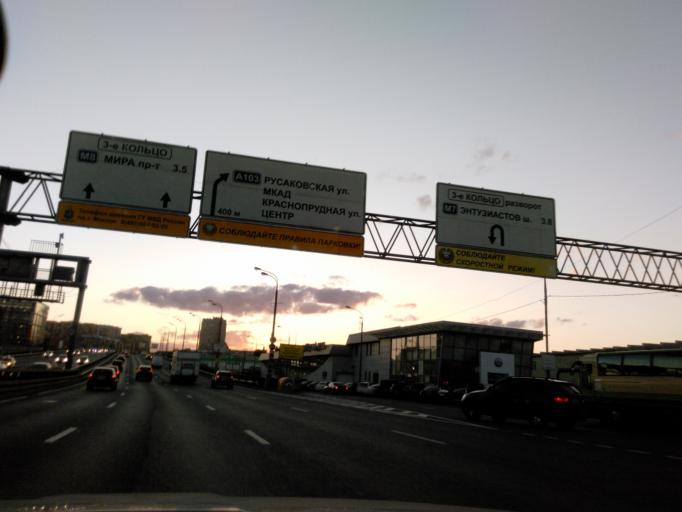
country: RU
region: Moscow
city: Lefortovo
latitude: 55.7774
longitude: 37.6800
